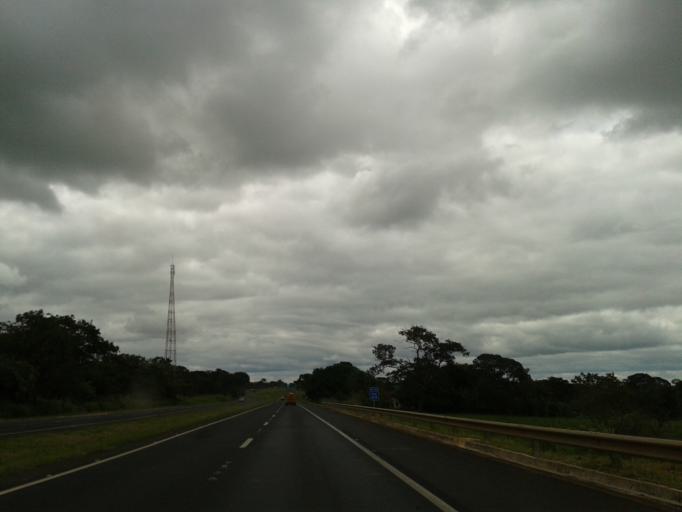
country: BR
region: Minas Gerais
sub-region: Monte Alegre De Minas
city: Monte Alegre de Minas
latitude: -18.8523
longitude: -48.7840
